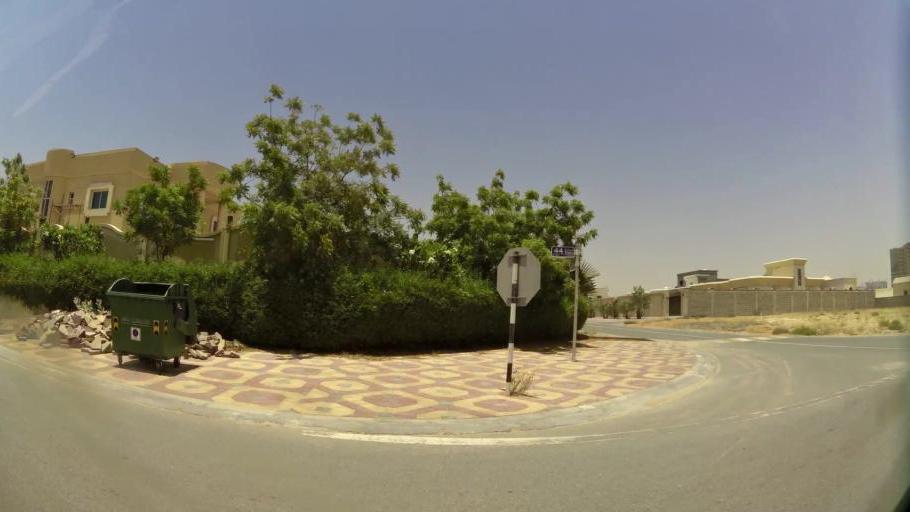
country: AE
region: Ajman
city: Ajman
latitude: 25.4079
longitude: 55.5040
